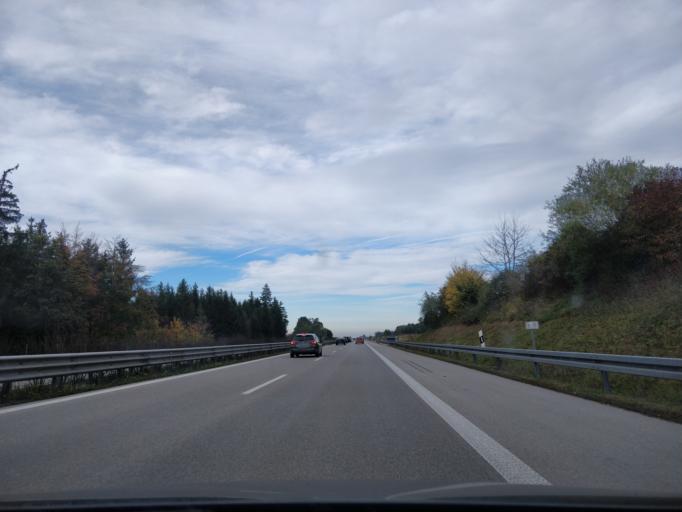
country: DE
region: Bavaria
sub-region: Upper Bavaria
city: Hurlach
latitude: 48.0988
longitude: 10.8373
